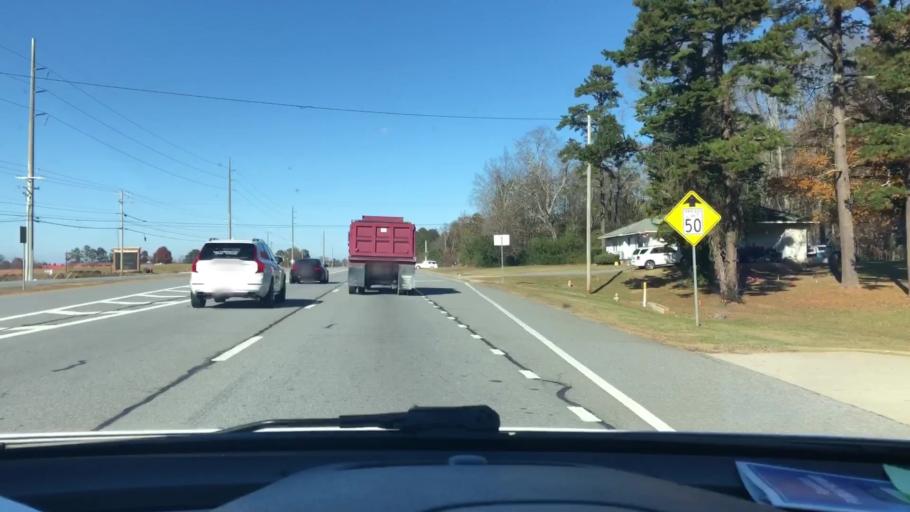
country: US
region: Georgia
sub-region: Fulton County
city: Johns Creek
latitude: 34.1081
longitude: -84.1765
